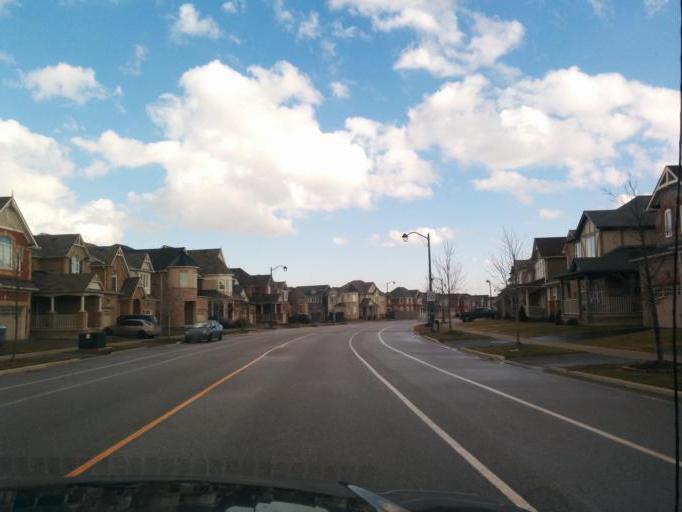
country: CA
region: Ontario
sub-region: Halton
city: Milton
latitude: 43.4841
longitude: -79.8691
